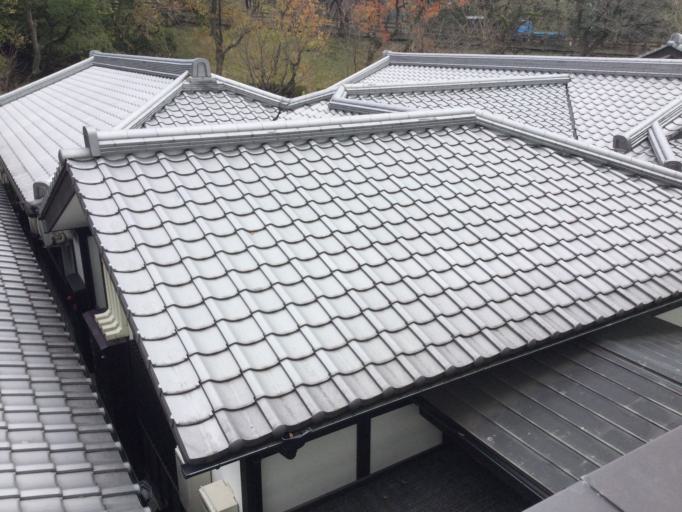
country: JP
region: Kumamoto
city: Kumamoto
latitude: 32.8043
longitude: 130.7037
